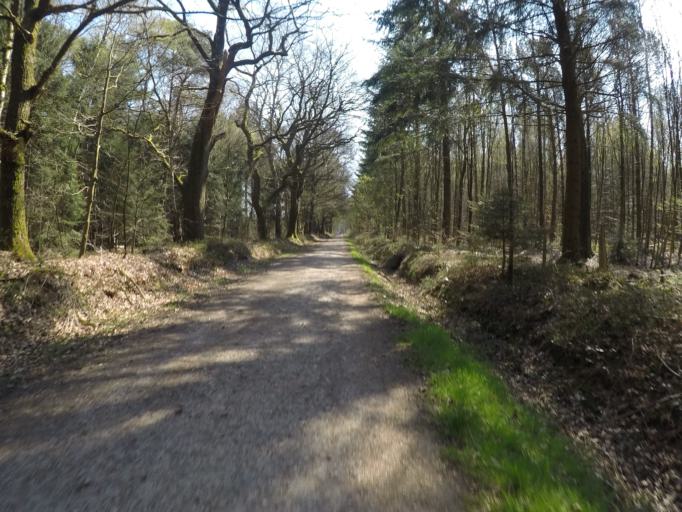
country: DE
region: Schleswig-Holstein
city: Appen
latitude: 53.6157
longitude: 9.7723
